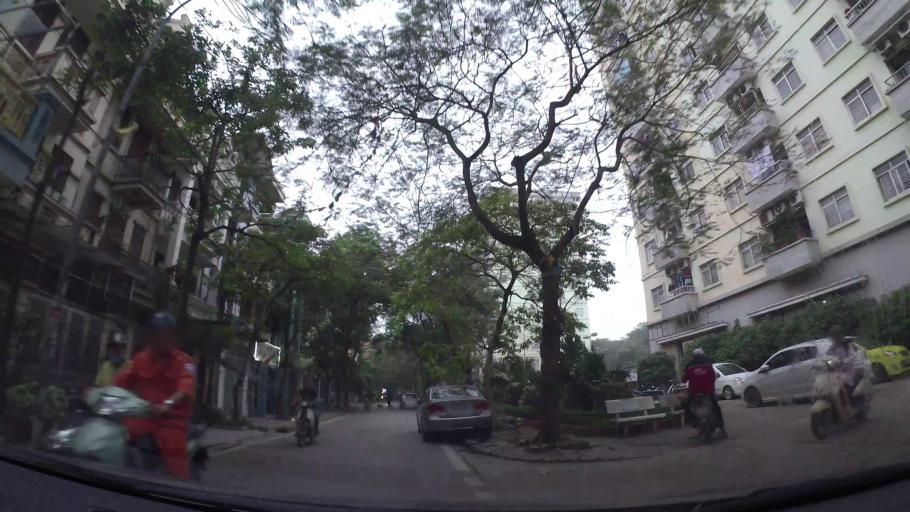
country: VN
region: Ha Noi
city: Thanh Xuan
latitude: 20.9871
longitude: 105.8279
